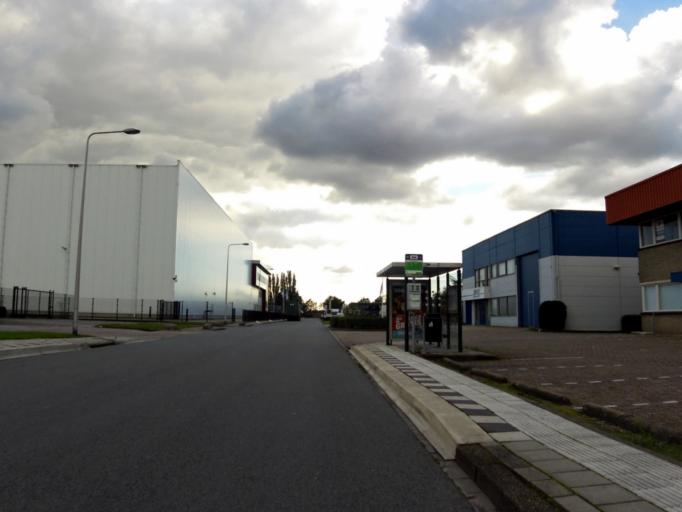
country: NL
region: South Holland
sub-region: Gemeente Leiderdorp
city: Leiderdorp
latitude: 52.1412
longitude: 4.5202
